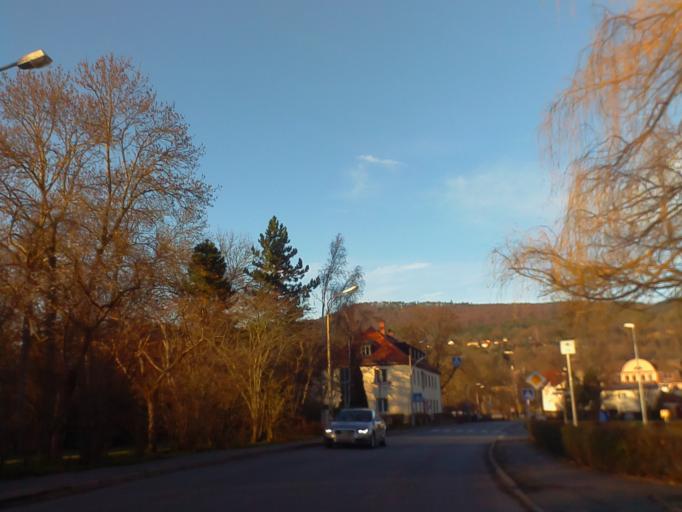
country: DE
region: Thuringia
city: Bad Blankenburg
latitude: 50.6793
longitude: 11.2735
